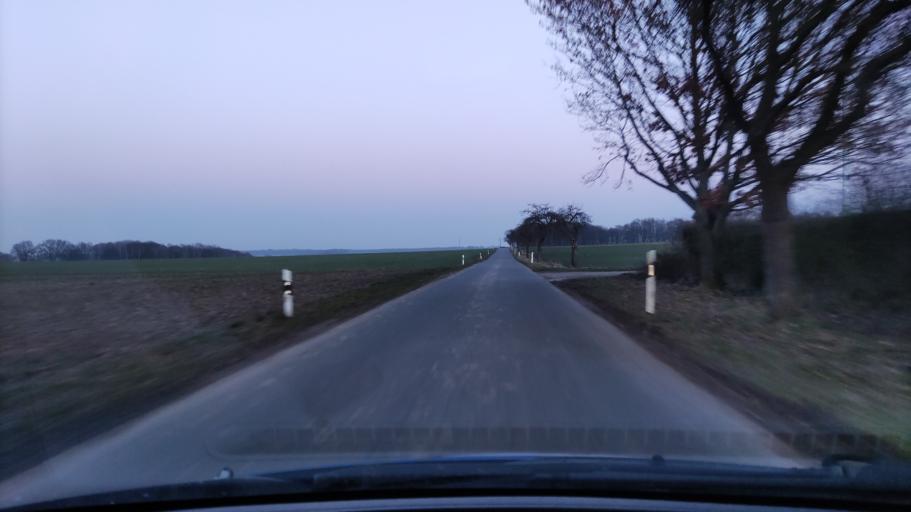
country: DE
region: Lower Saxony
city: Barum
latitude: 53.0551
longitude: 10.4892
